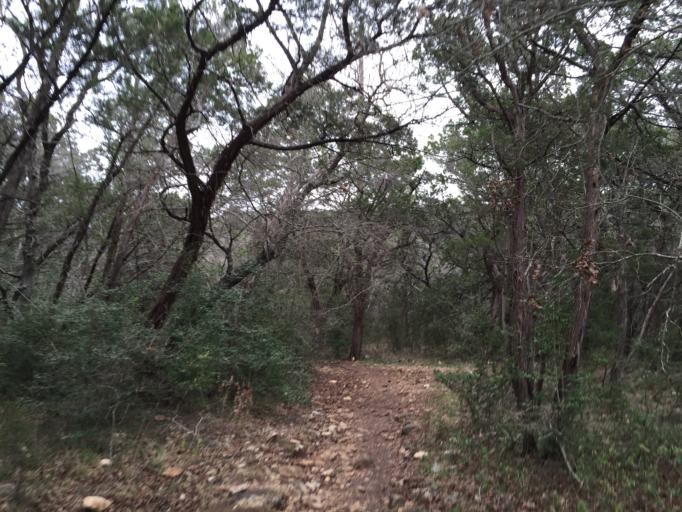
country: US
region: Texas
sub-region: Travis County
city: Rollingwood
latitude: 30.2466
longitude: -97.8217
